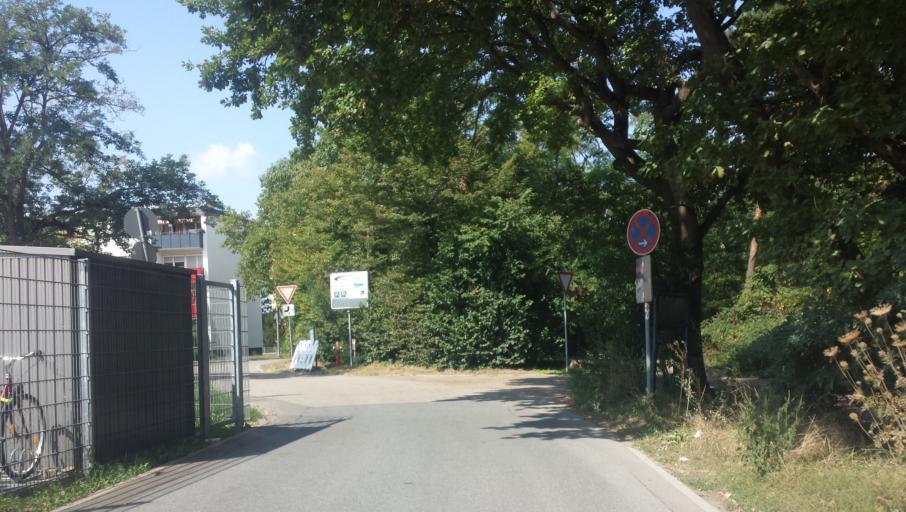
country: DE
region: Baden-Wuerttemberg
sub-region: Karlsruhe Region
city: Hockenheim
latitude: 49.3188
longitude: 8.5647
